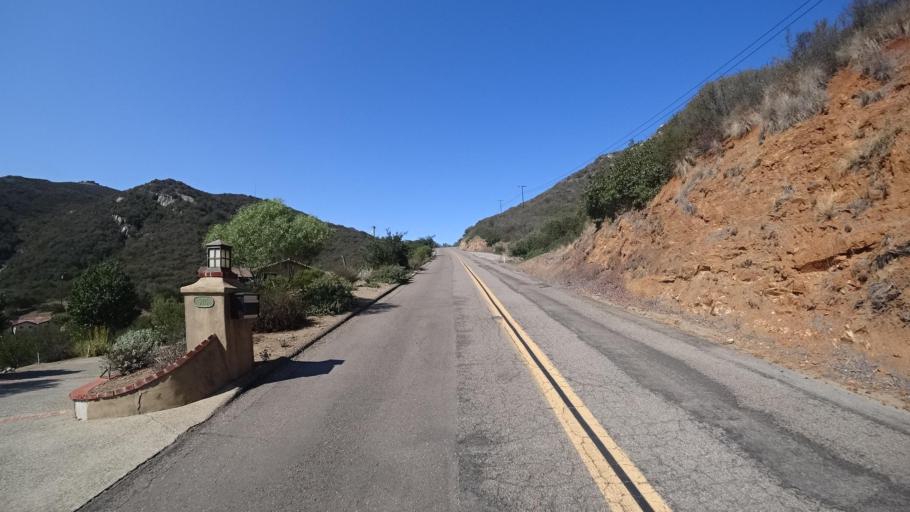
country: US
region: California
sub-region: San Diego County
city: Escondido
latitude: 33.0602
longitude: -117.1313
